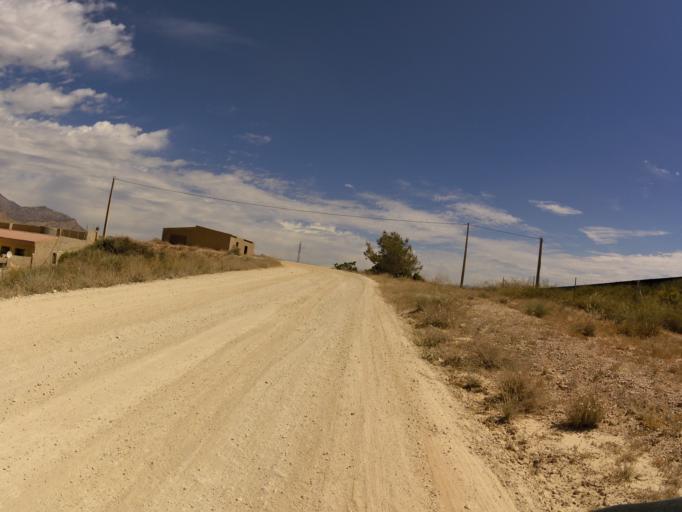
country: ES
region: Valencia
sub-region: Provincia de Alicante
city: Agost
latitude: 38.3980
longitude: -0.6099
